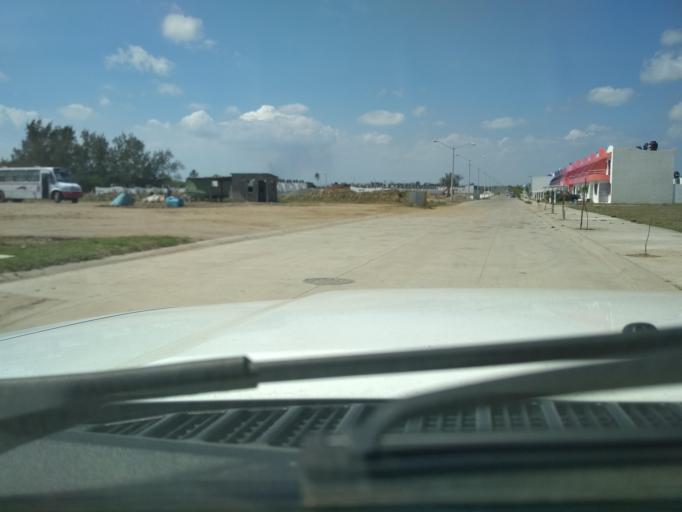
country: MX
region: Veracruz
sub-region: Veracruz
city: Las Amapolas
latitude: 19.1329
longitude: -96.2022
